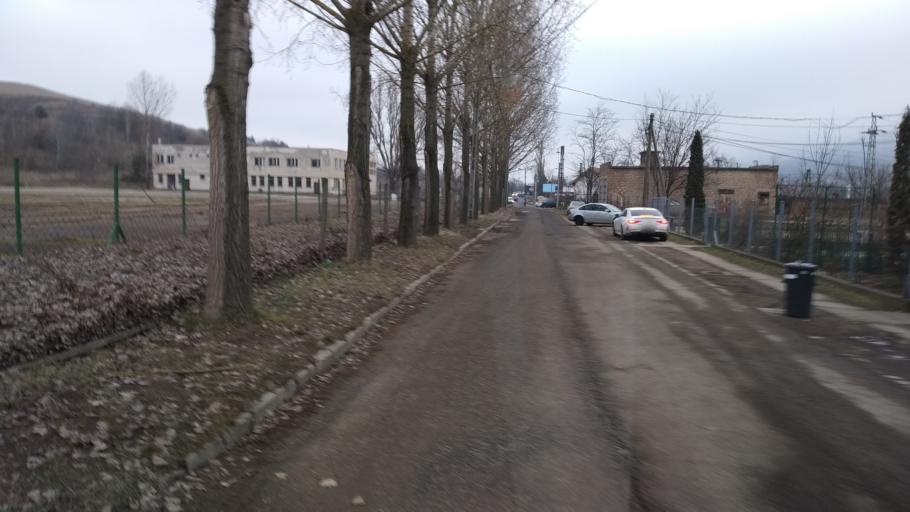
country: HU
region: Pest
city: Pilisborosjeno
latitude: 47.5974
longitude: 18.9767
